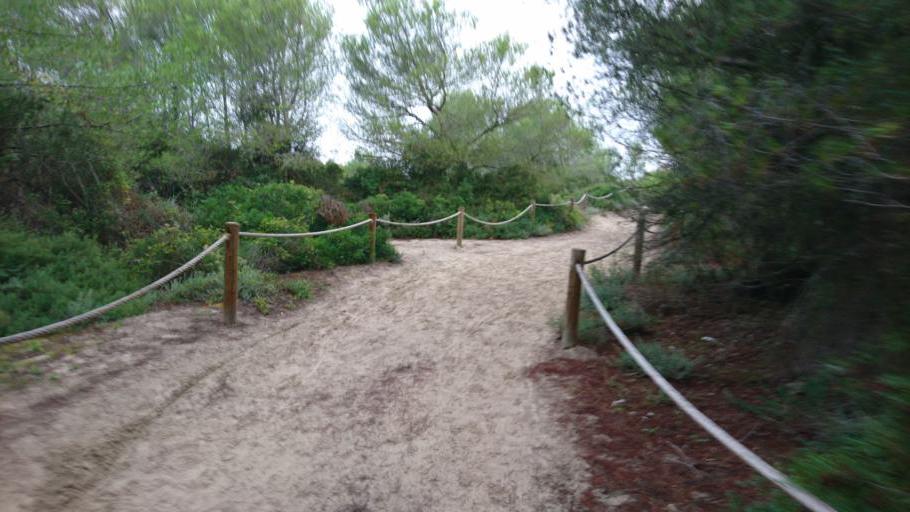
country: ES
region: Balearic Islands
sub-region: Illes Balears
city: Port d'Alcudia
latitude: 39.7756
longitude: 3.1394
